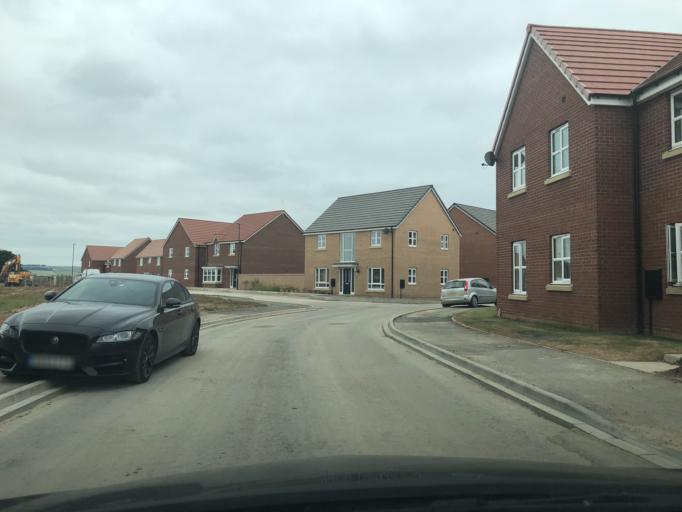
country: GB
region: England
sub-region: North Yorkshire
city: East Ayton
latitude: 54.2431
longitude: -0.4885
